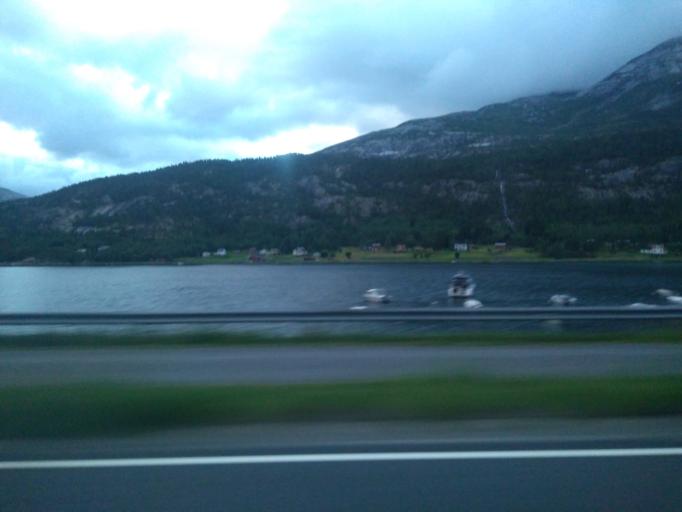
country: NO
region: Nordland
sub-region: Sorfold
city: Straumen
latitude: 67.7052
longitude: 15.8487
